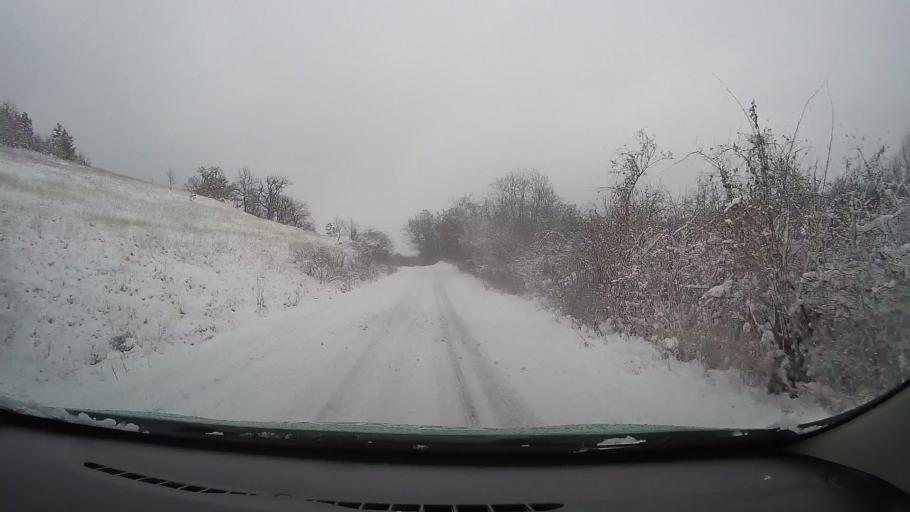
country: RO
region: Hunedoara
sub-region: Comuna Pestisu Mic
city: Pestisu Mic
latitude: 45.8235
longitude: 22.8629
